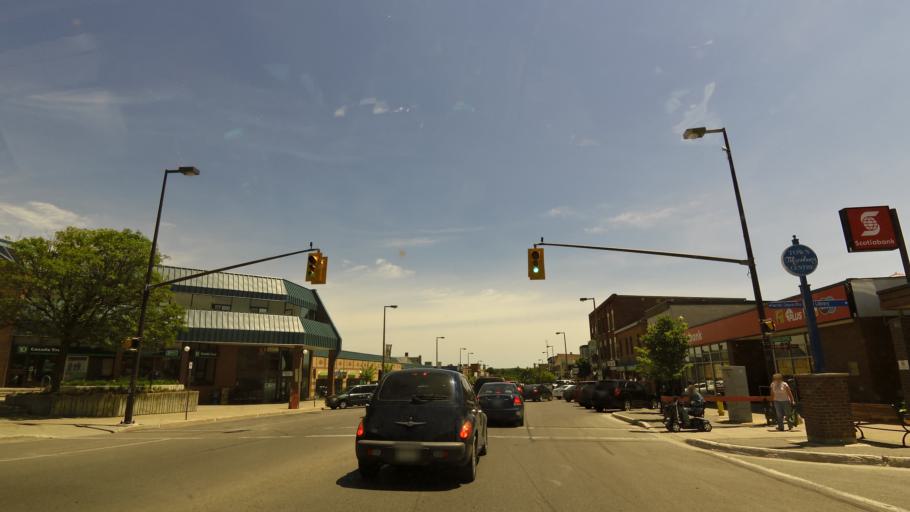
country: CA
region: Ontario
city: Ingersoll
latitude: 42.8620
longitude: -80.7293
